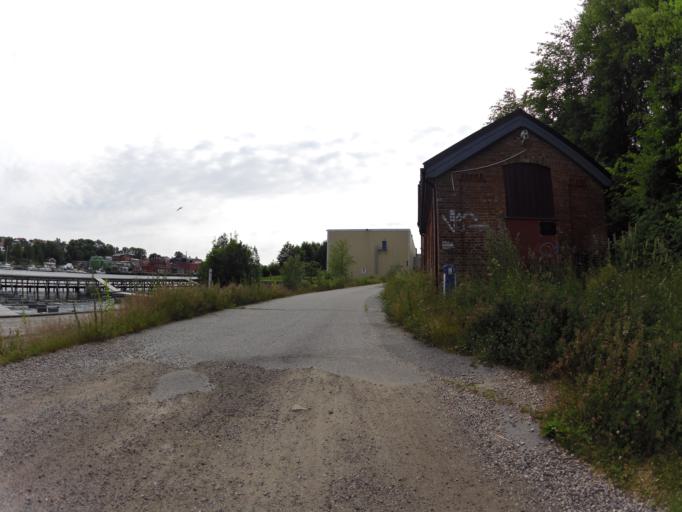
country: NO
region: Ostfold
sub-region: Fredrikstad
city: Fredrikstad
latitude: 59.2194
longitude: 10.9671
